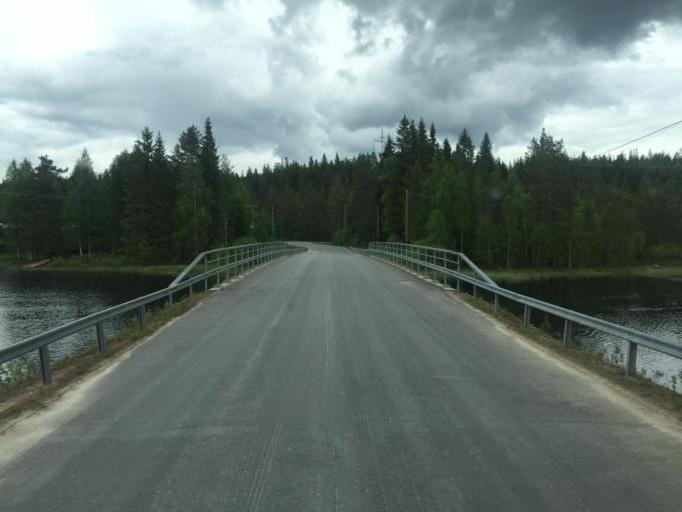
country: SE
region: Dalarna
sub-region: Malung-Saelens kommun
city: Malung
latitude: 60.4558
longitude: 13.7486
